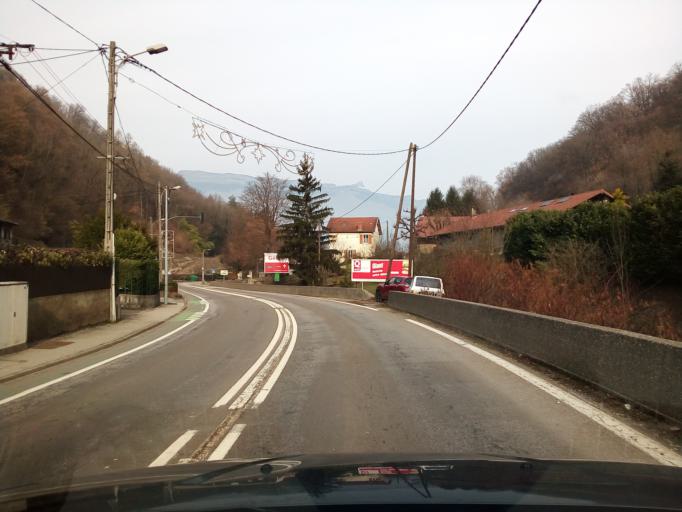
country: FR
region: Rhone-Alpes
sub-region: Departement de l'Isere
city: Gieres
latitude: 45.1749
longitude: 5.7901
